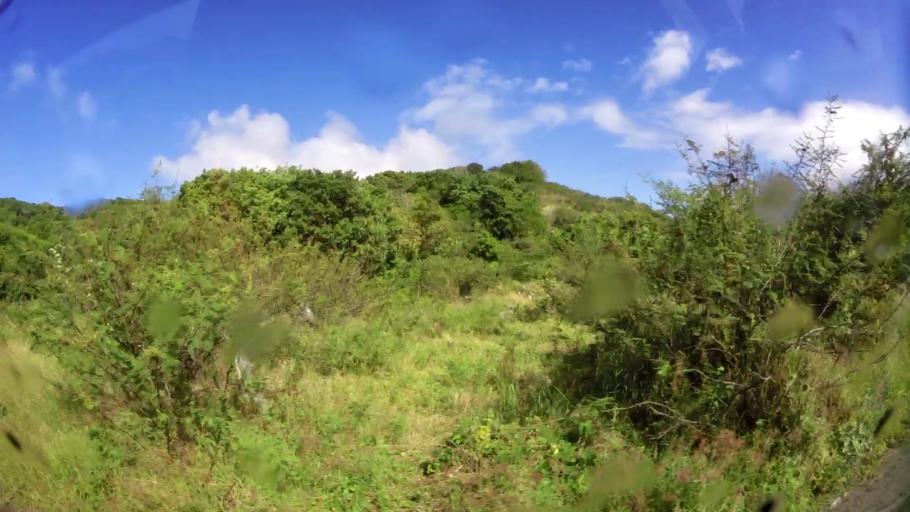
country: MS
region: Saint Peter
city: Saint Peters
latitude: 16.7428
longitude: -62.2245
